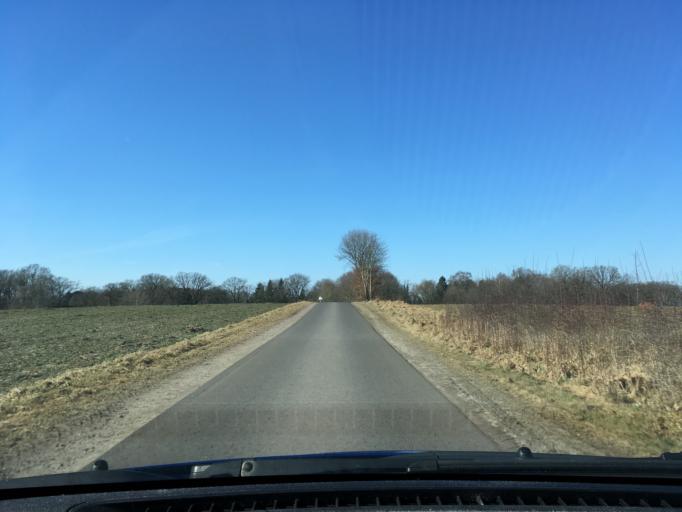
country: DE
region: Lower Saxony
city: Schneverdingen
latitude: 53.0828
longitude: 9.7734
